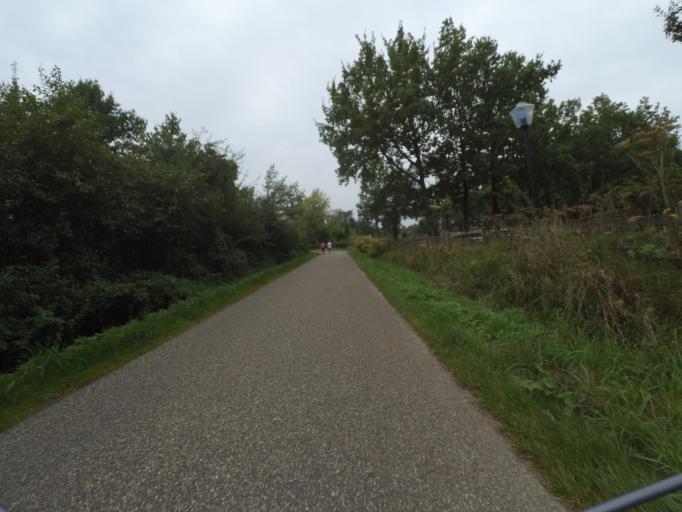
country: NL
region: Overijssel
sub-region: Gemeente Oldenzaal
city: Oldenzaal
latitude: 52.3197
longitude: 6.9573
